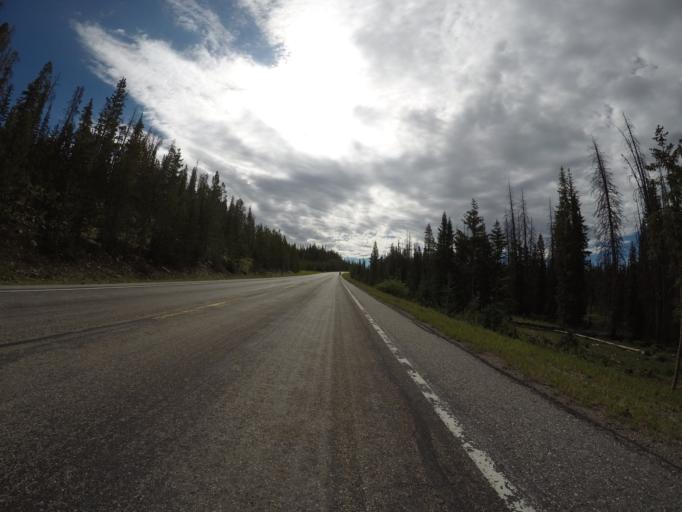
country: US
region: Wyoming
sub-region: Carbon County
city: Saratoga
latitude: 41.3256
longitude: -106.4279
